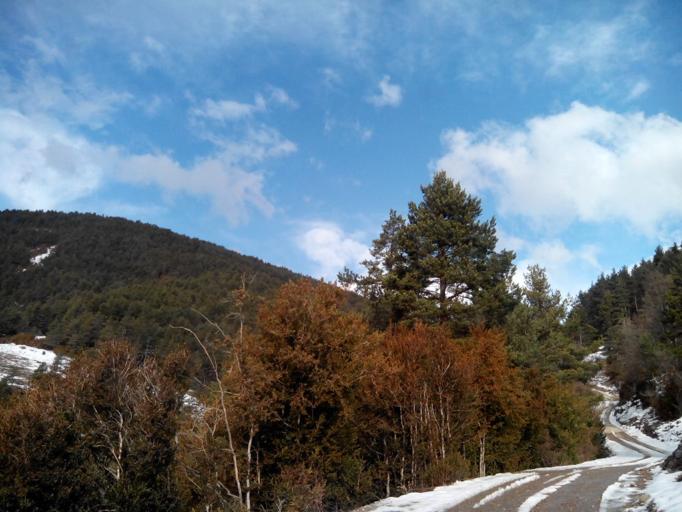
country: ES
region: Catalonia
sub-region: Provincia de Barcelona
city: Vilada
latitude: 42.1870
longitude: 1.9281
